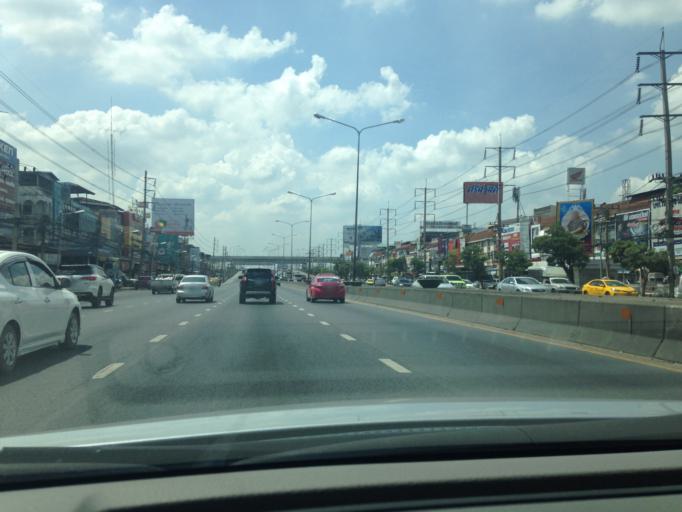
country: TH
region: Phra Nakhon Si Ayutthaya
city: Ban Bang Kadi Pathum Thani
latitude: 13.9868
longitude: 100.6070
